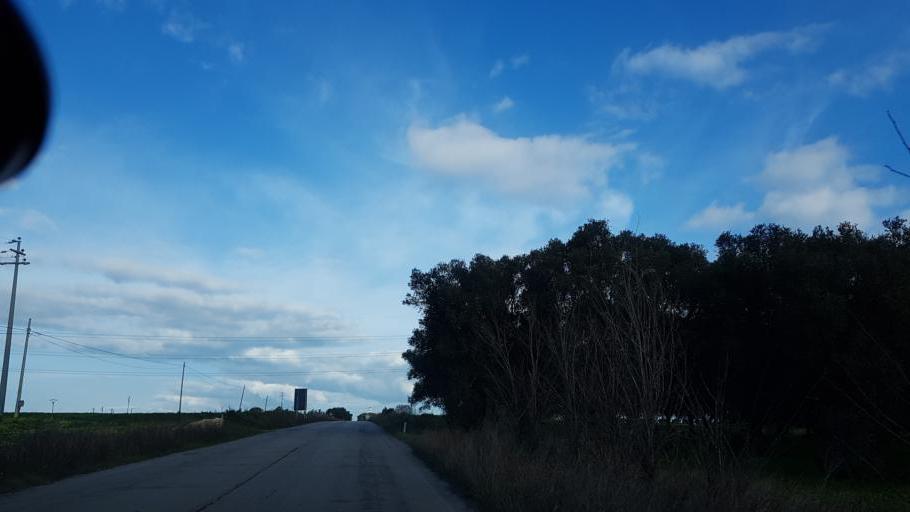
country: IT
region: Apulia
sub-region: Provincia di Brindisi
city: La Rosa
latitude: 40.5908
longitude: 17.9606
